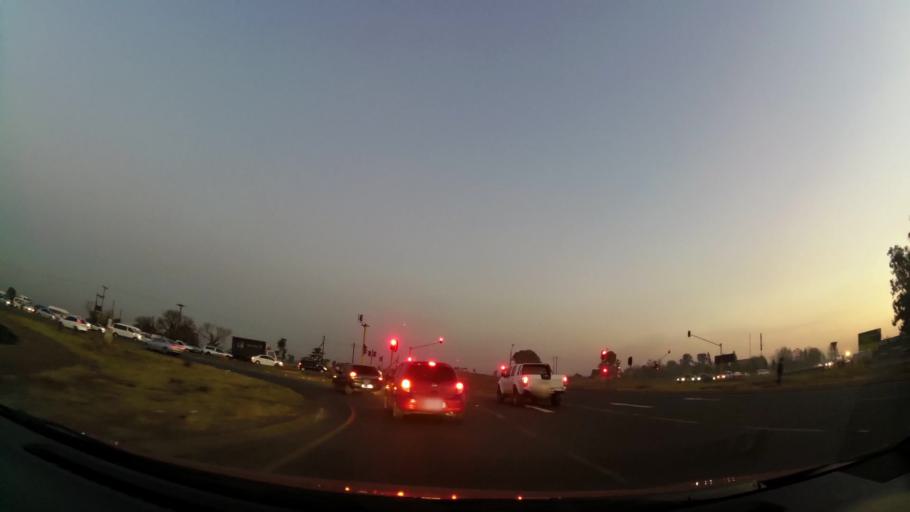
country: ZA
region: Gauteng
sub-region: City of Johannesburg Metropolitan Municipality
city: Soweto
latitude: -26.2988
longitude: 27.8158
